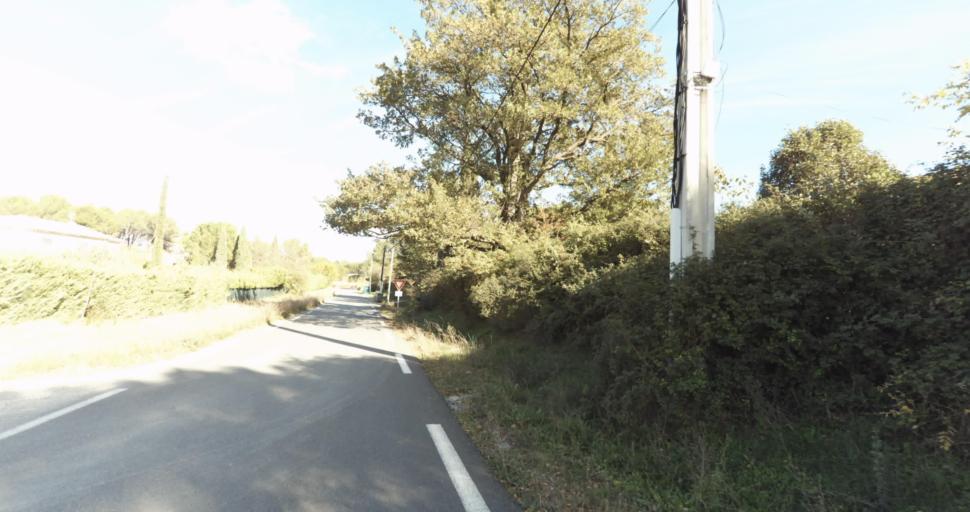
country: FR
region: Provence-Alpes-Cote d'Azur
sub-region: Departement des Bouches-du-Rhone
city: Venelles
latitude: 43.6085
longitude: 5.4939
